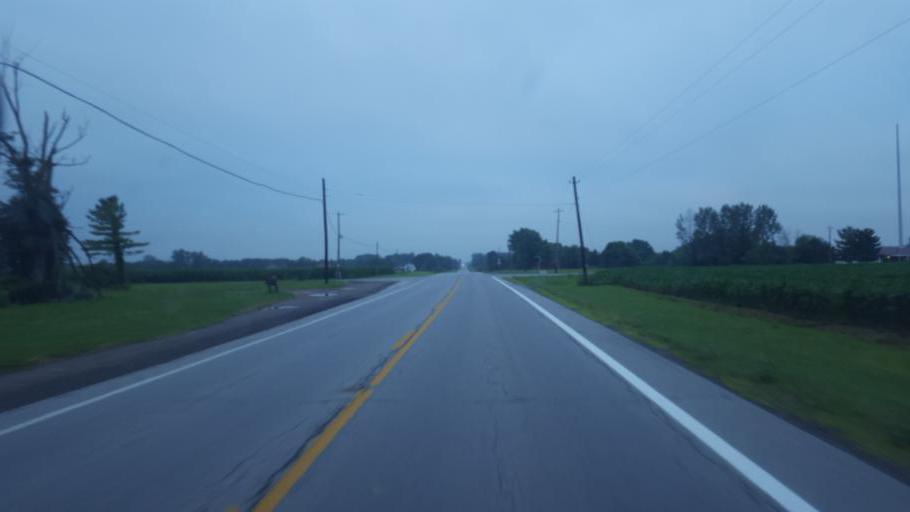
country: US
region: Ohio
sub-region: Madison County
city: Mount Sterling
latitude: 39.6828
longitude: -83.2999
